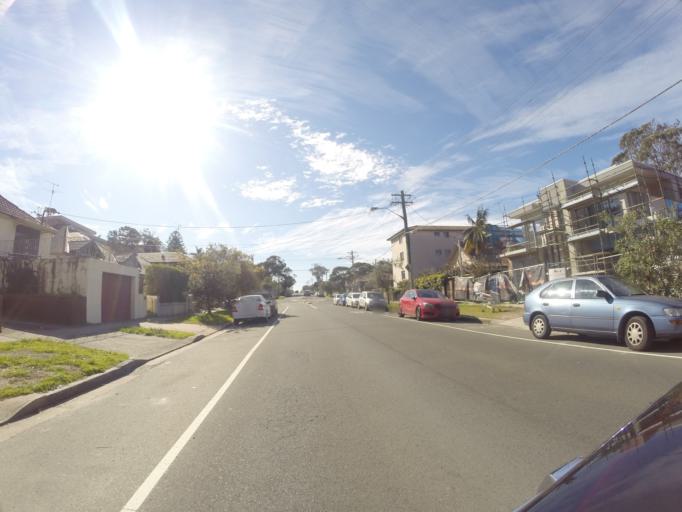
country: AU
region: New South Wales
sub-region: Randwick
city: South Coogee
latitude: -33.9265
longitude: 151.2507
